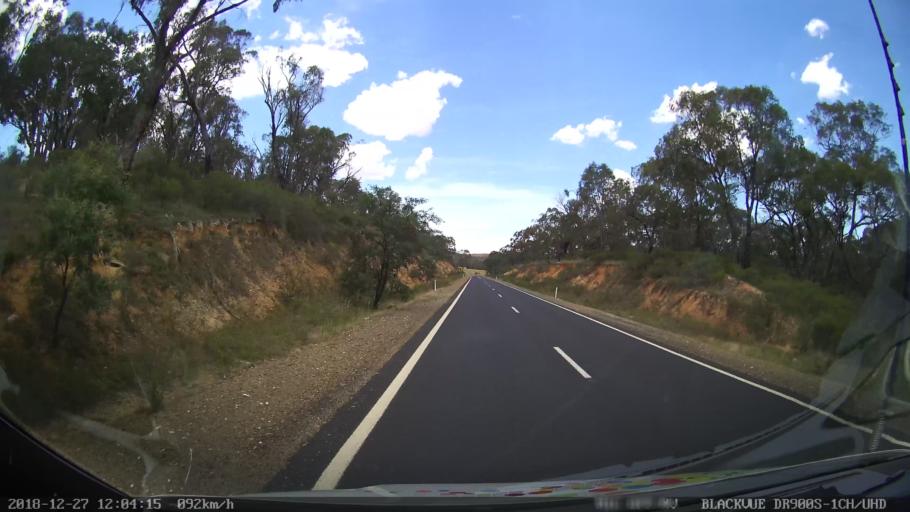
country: AU
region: New South Wales
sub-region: Blayney
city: Blayney
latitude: -33.7952
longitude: 149.3525
